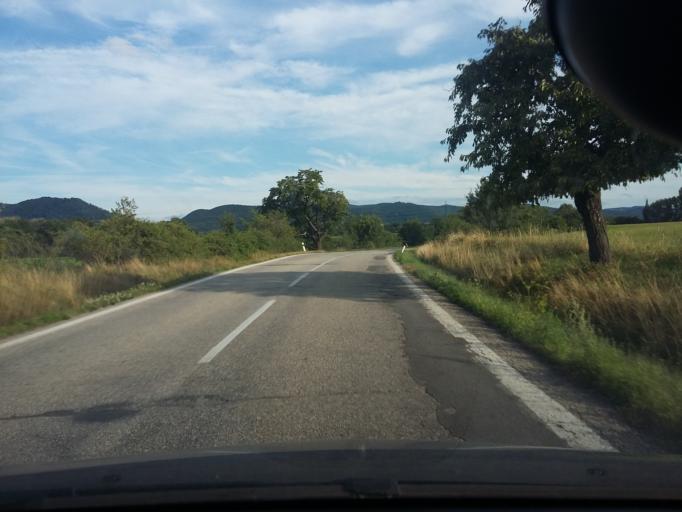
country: SK
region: Bratislavsky
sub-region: Okres Malacky
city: Malacky
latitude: 48.4377
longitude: 17.1585
